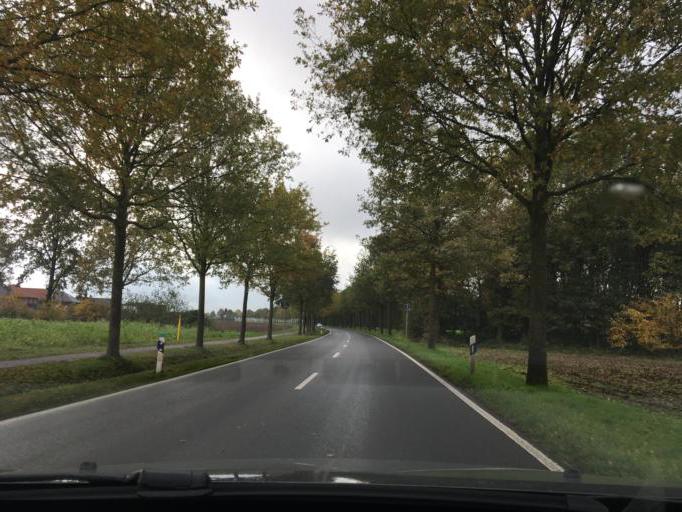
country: DE
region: North Rhine-Westphalia
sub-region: Regierungsbezirk Munster
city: Vreden
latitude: 52.0472
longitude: 6.8060
